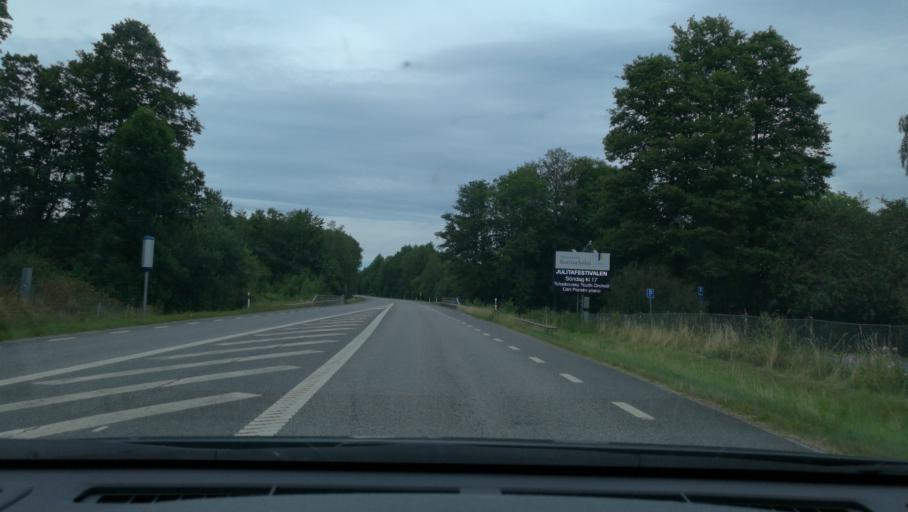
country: SE
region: Soedermanland
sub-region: Katrineholms Kommun
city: Katrineholm
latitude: 58.9672
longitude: 16.1972
